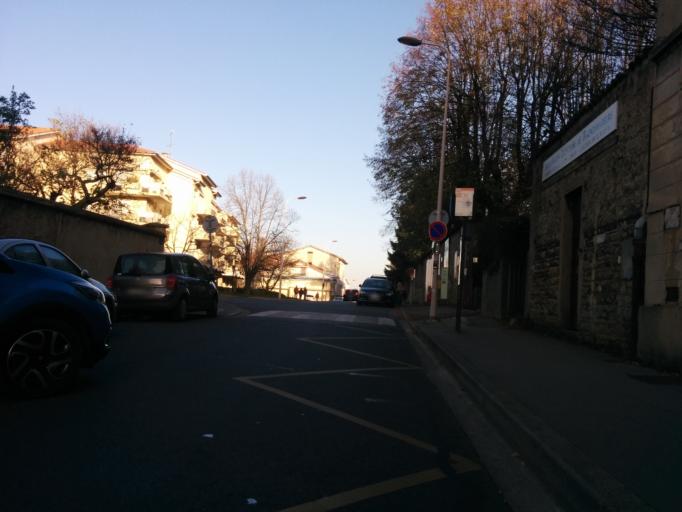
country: FR
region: Rhone-Alpes
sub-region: Departement du Rhone
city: Tassin-la-Demi-Lune
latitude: 45.7596
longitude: 4.8159
